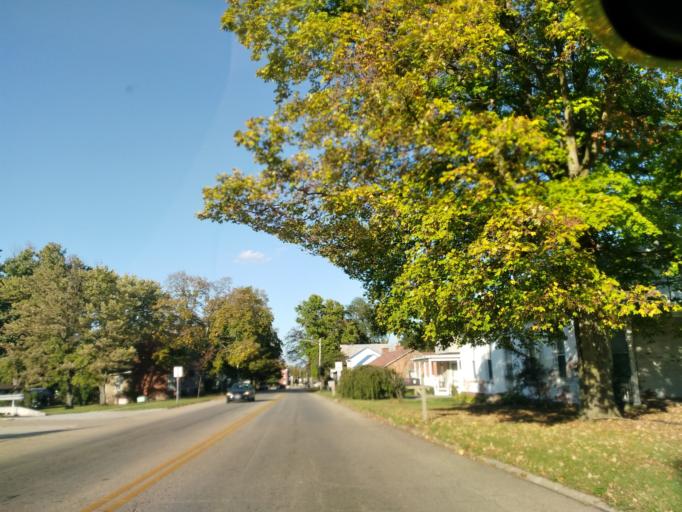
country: US
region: Ohio
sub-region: Ross County
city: Kingston
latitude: 39.4741
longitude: -82.9101
